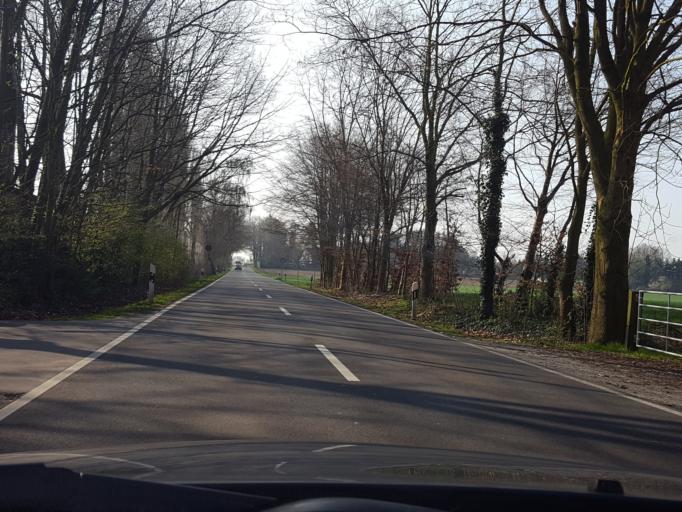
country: DE
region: North Rhine-Westphalia
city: Oer-Erkenschwick
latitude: 51.6346
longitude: 7.2424
